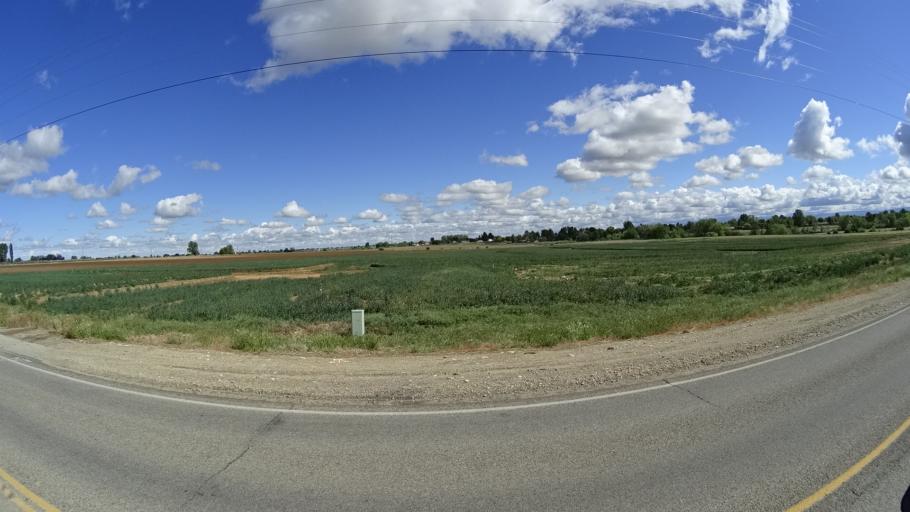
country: US
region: Idaho
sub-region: Ada County
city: Kuna
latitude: 43.4879
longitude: -116.4416
